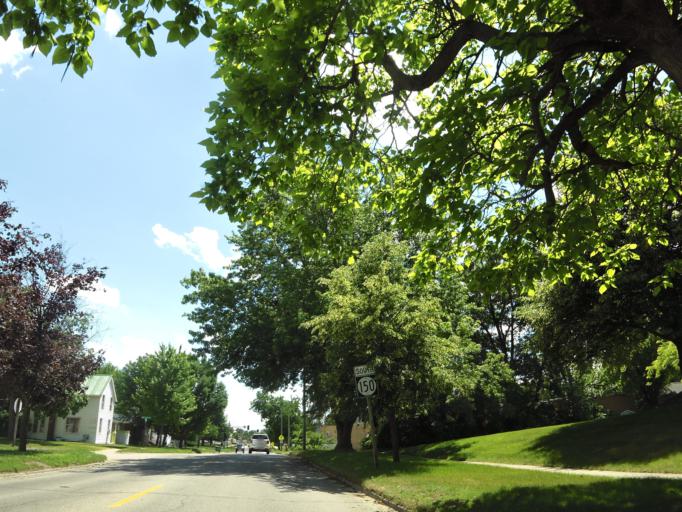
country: US
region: Iowa
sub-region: Buchanan County
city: Independence
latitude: 42.4723
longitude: -91.8894
